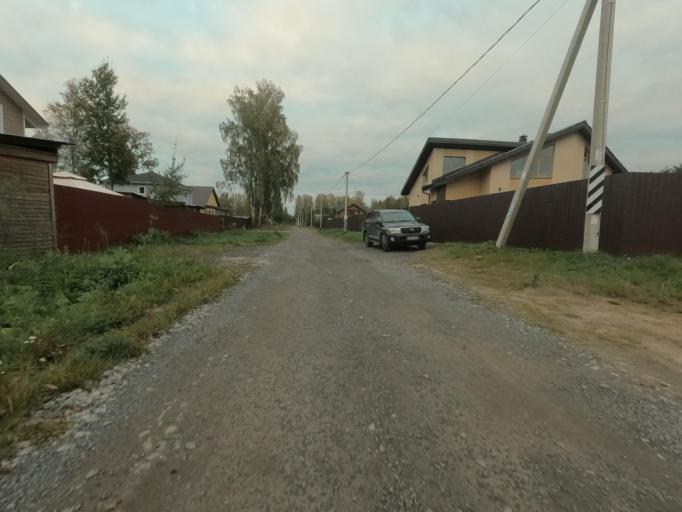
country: RU
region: Leningrad
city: Pavlovo
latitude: 59.8092
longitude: 30.9203
